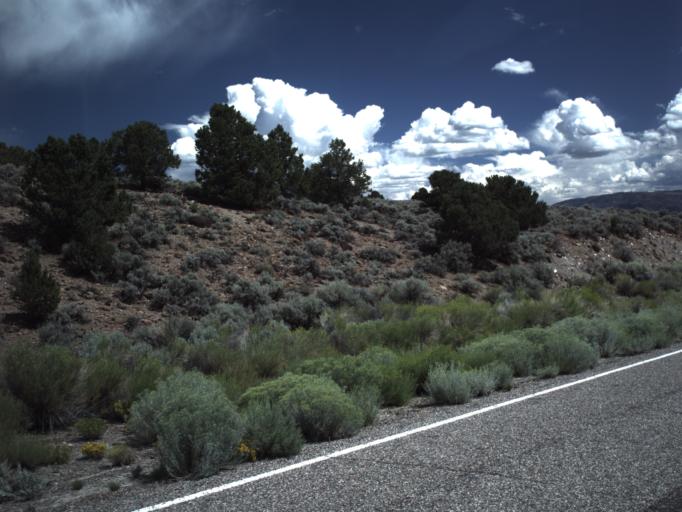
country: US
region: Utah
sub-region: Piute County
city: Junction
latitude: 38.2602
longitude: -112.2593
